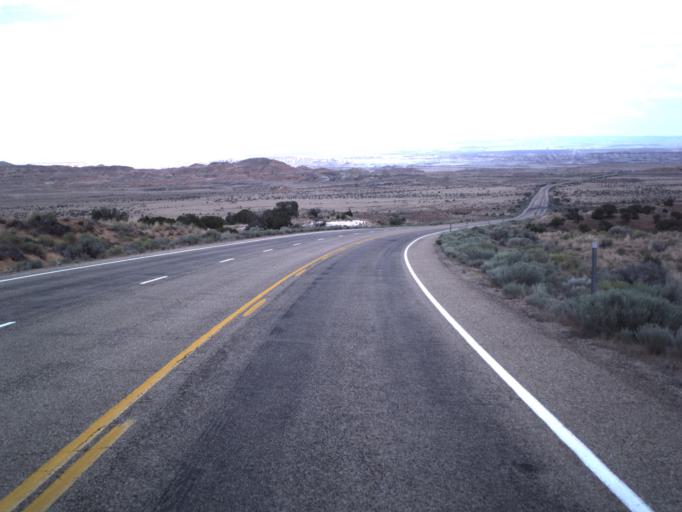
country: US
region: Utah
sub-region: Uintah County
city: Naples
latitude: 40.1409
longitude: -109.2740
